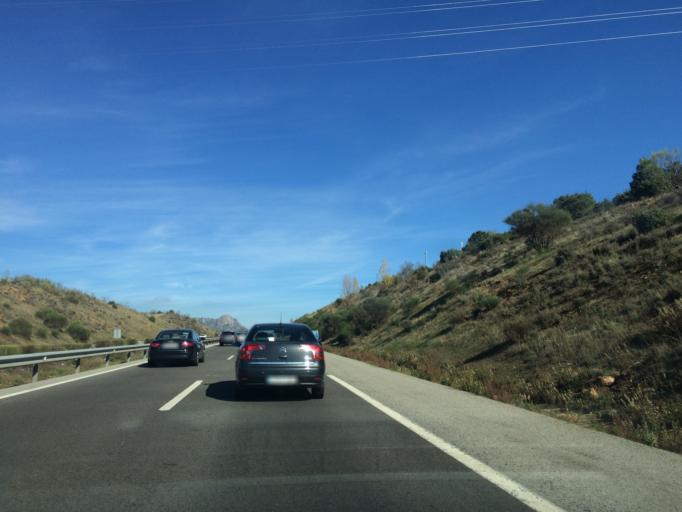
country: ES
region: Madrid
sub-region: Provincia de Madrid
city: Cabanillas de la Sierra
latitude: 40.8150
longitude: -3.6162
